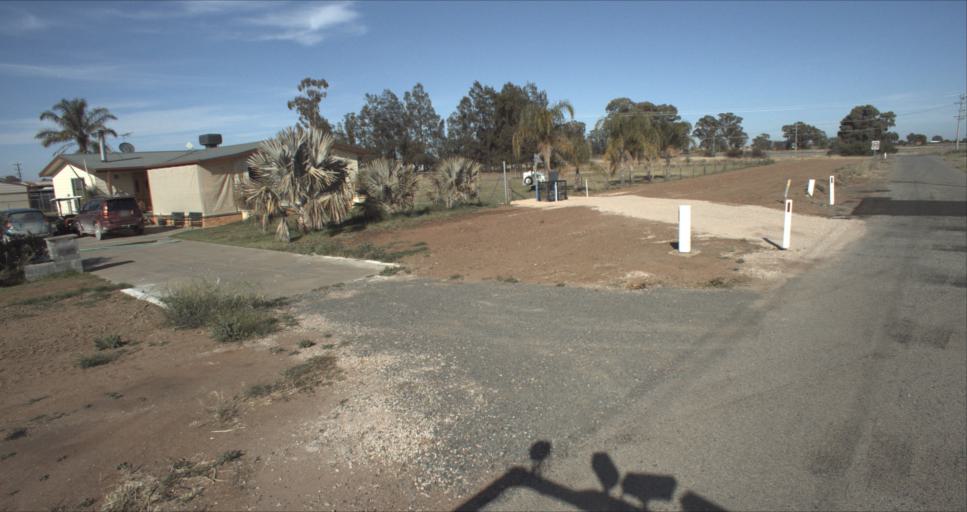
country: AU
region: New South Wales
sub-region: Leeton
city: Leeton
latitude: -34.5960
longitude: 146.4068
